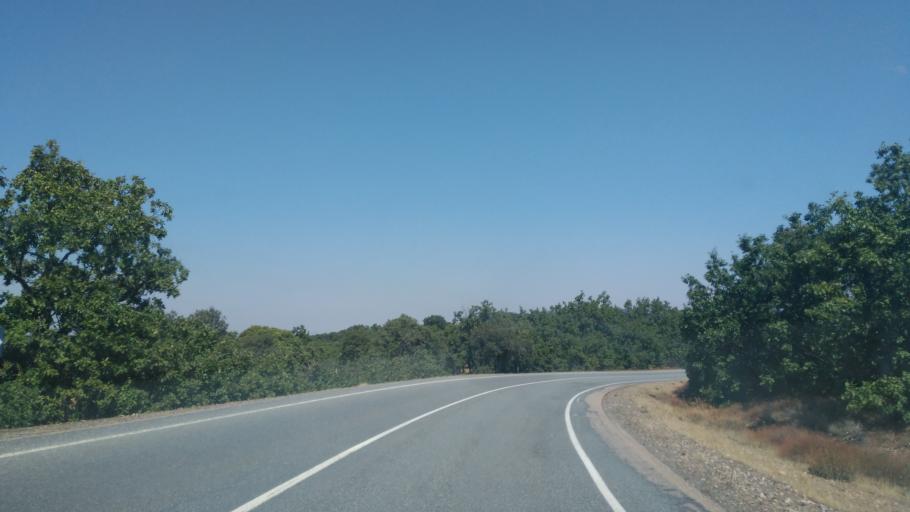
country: ES
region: Castille and Leon
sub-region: Provincia de Salamanca
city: Aldeanueva de la Sierra
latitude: 40.6000
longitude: -6.0938
